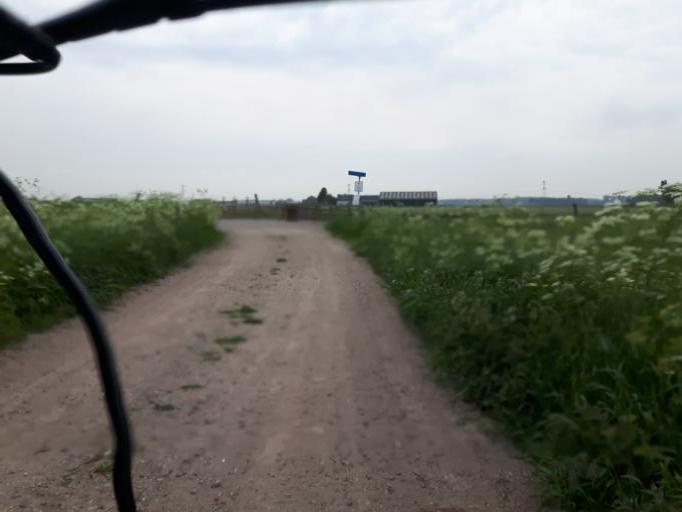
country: NL
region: North Brabant
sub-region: Gemeente Steenbergen
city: Welberg
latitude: 51.5545
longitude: 4.3240
